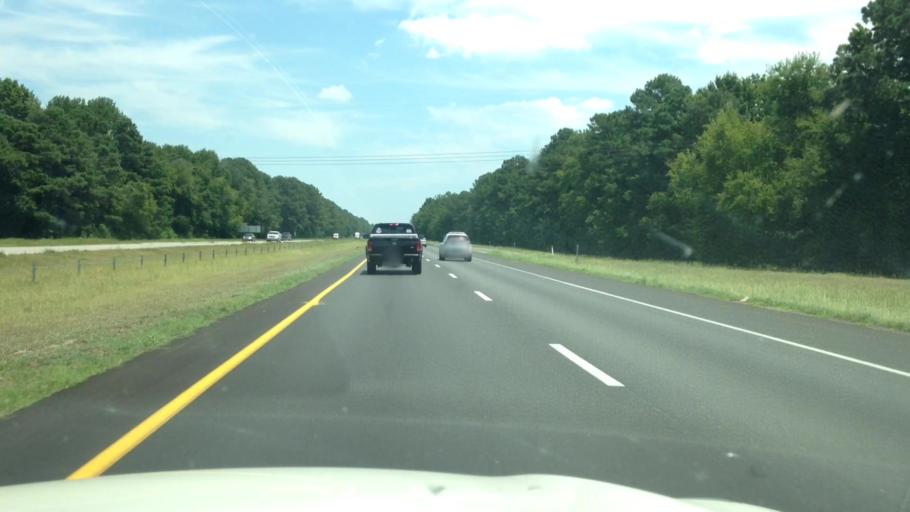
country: US
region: South Carolina
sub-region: Lee County
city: Bishopville
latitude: 34.1900
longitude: -80.1632
